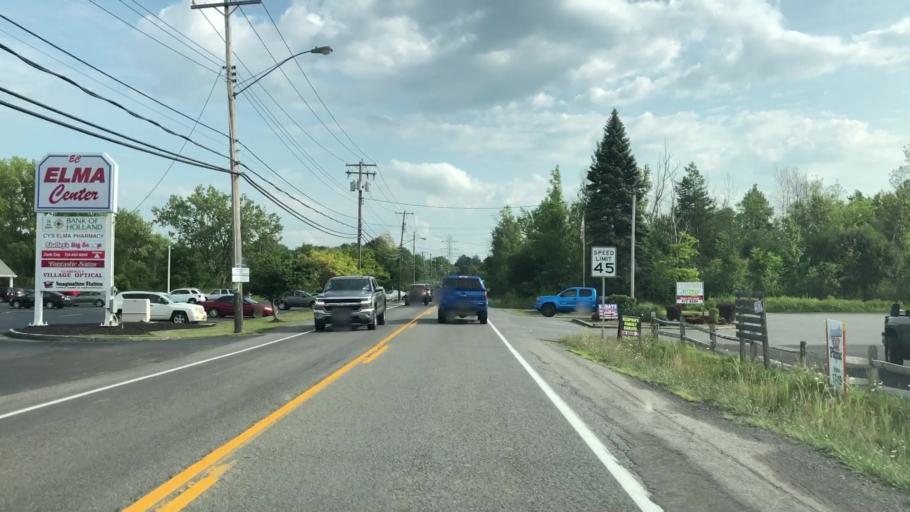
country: US
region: New York
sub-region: Erie County
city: Elma Center
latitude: 42.8351
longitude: -78.6369
